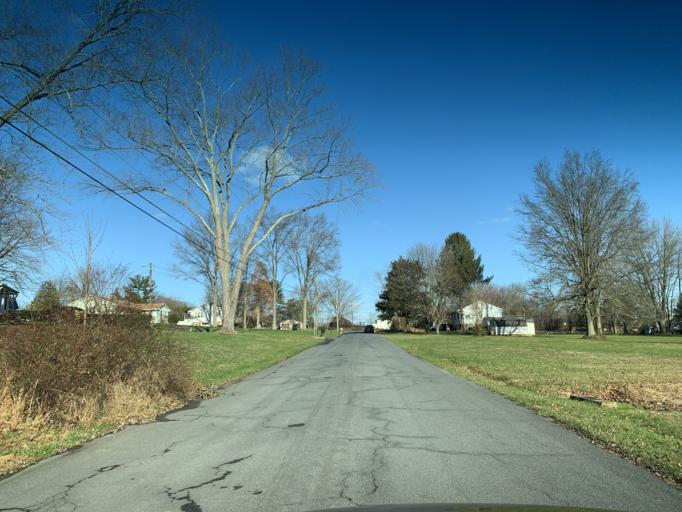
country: US
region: Maryland
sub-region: Harford County
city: Bel Air South
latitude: 39.5549
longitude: -76.2585
